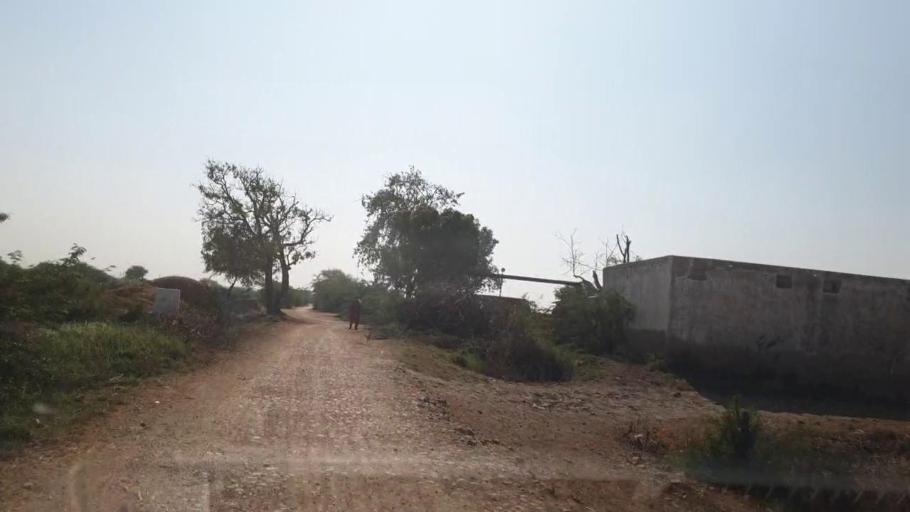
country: PK
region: Sindh
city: Gharo
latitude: 24.6788
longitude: 67.7501
